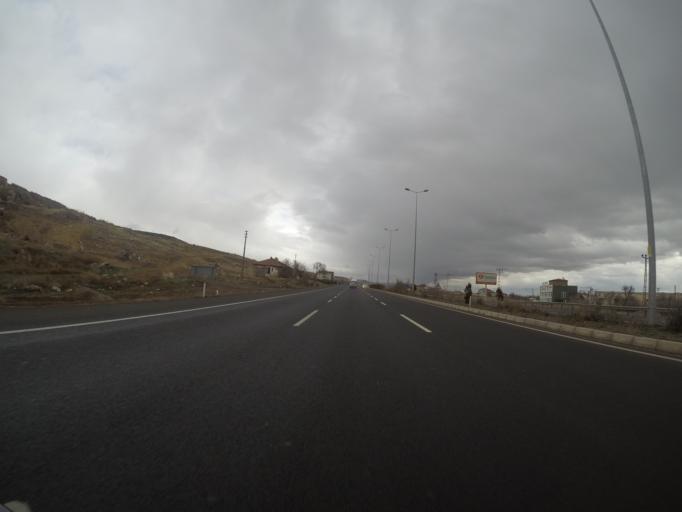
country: TR
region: Kayseri
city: Incesu
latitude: 38.7324
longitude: 35.2850
